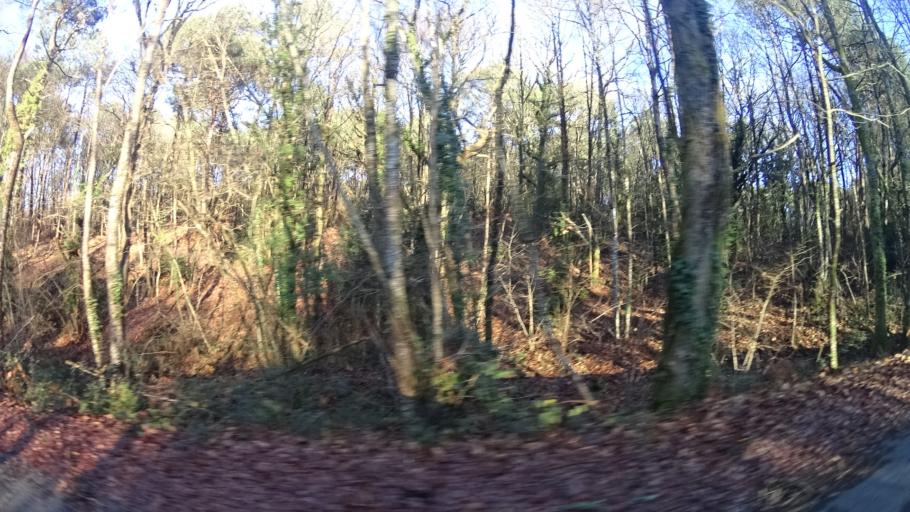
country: FR
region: Brittany
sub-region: Departement du Morbihan
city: Allaire
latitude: 47.6621
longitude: -2.1588
